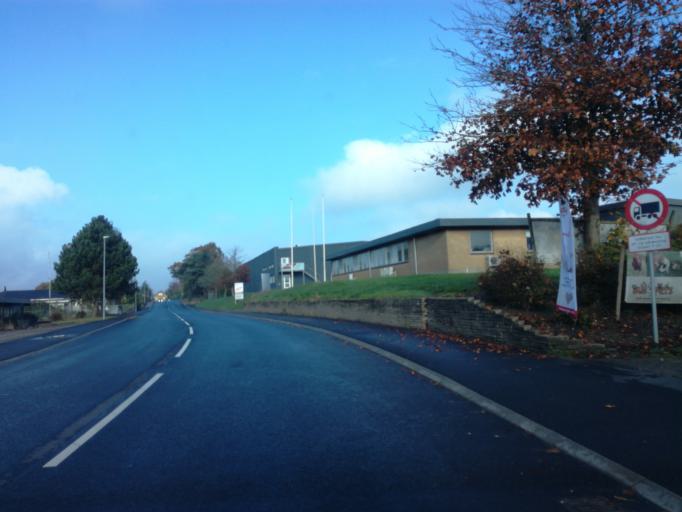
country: DK
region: South Denmark
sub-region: Vejle Kommune
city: Borkop
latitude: 55.6438
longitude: 9.6615
